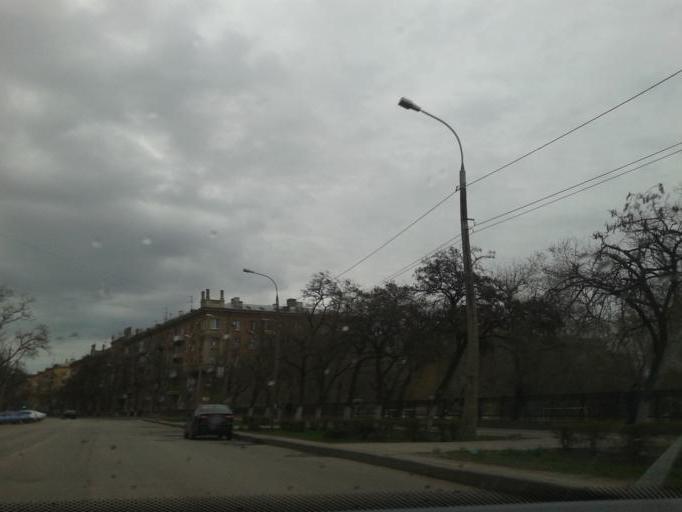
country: RU
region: Volgograd
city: Volgograd
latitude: 48.7097
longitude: 44.5260
